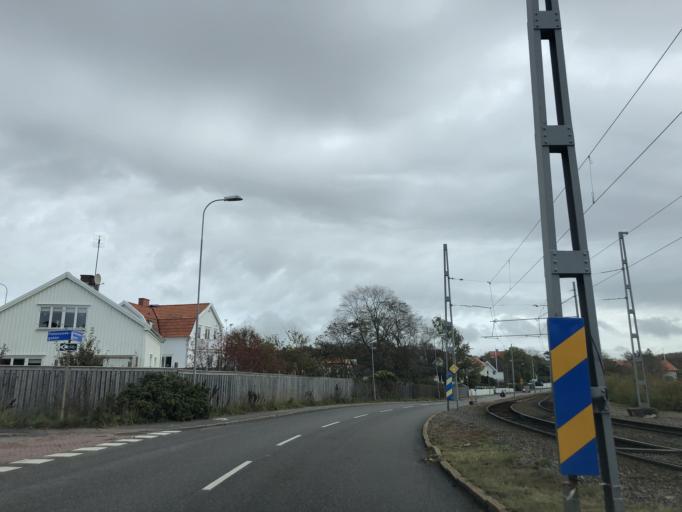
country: SE
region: Vaestra Goetaland
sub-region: Goteborg
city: Majorna
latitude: 57.6694
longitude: 11.8557
